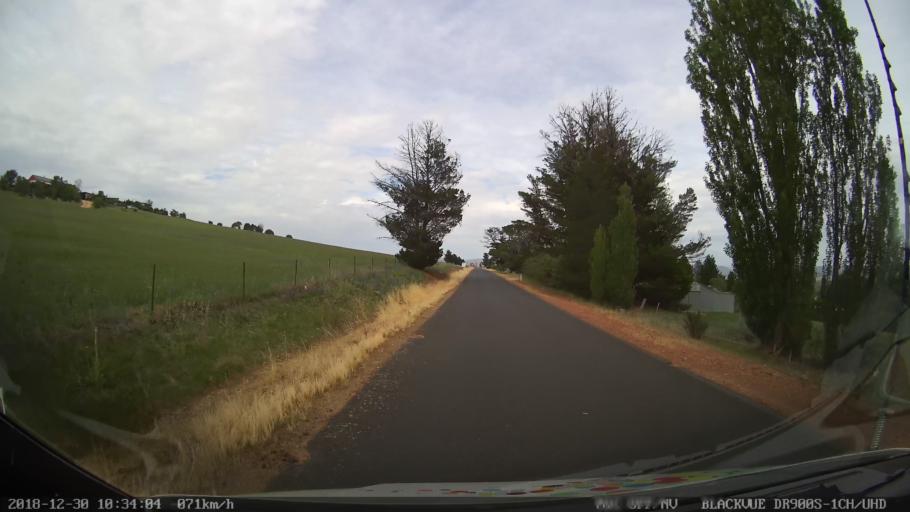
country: AU
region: New South Wales
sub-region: Snowy River
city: Berridale
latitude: -36.4995
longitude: 148.8449
